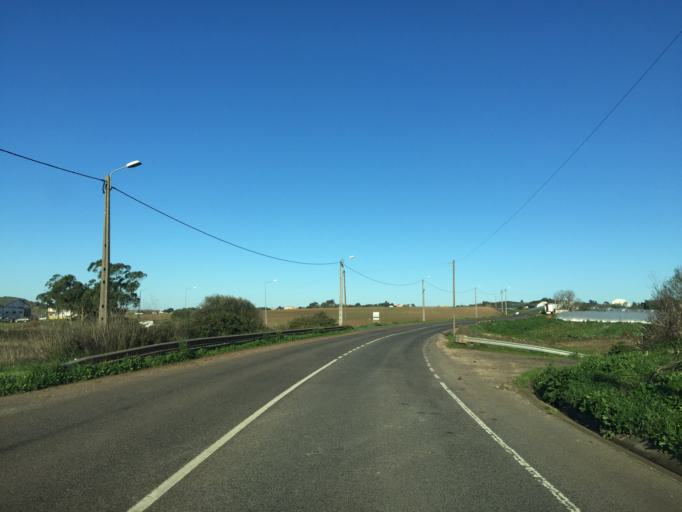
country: PT
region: Lisbon
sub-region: Sintra
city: Almargem
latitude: 38.8577
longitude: -9.2766
